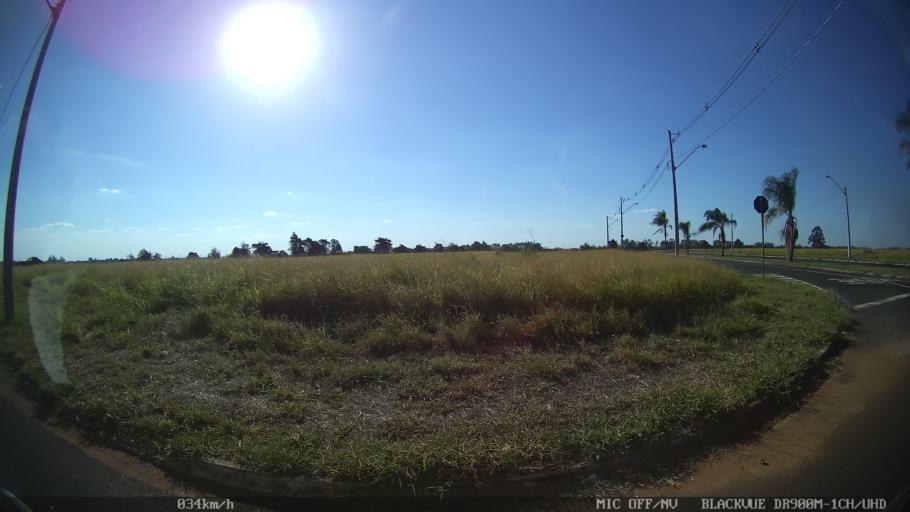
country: BR
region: Sao Paulo
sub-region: Franca
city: Franca
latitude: -20.5062
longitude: -47.4369
